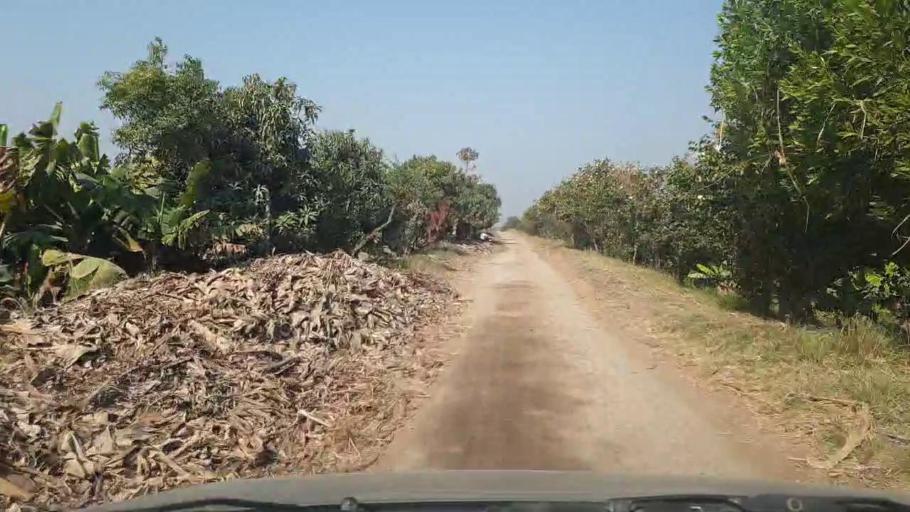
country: PK
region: Sindh
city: Mirwah Gorchani
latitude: 25.2487
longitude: 69.1076
